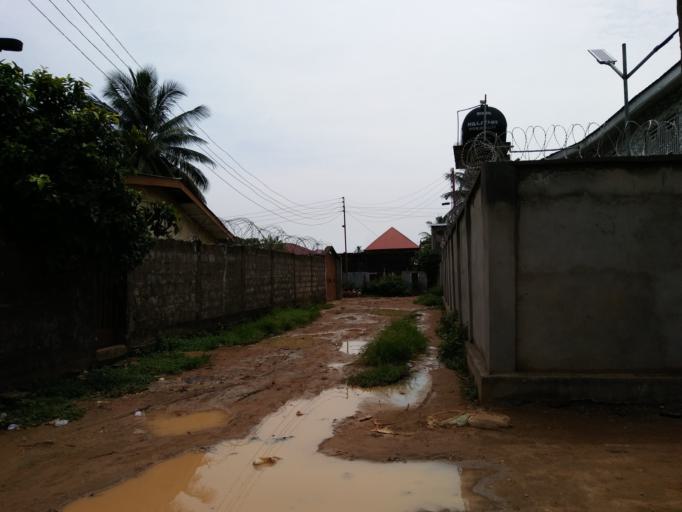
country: SL
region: Western Area
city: Hastings
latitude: 8.3834
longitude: -13.1485
